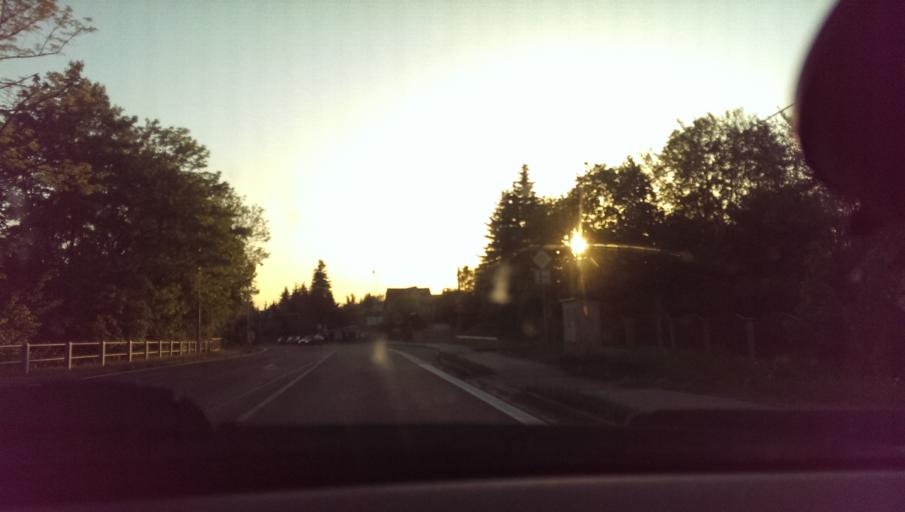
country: CZ
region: Zlin
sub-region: Okres Vsetin
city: Roznov pod Radhostem
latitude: 49.4656
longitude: 18.1564
